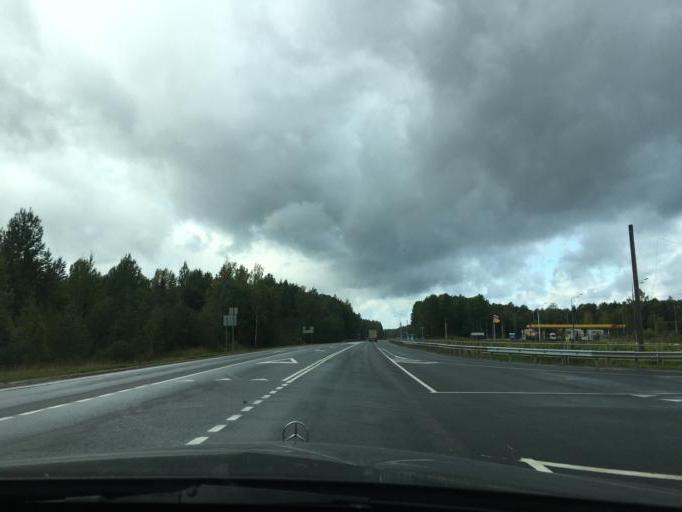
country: RU
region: Tverskaya
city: Nelidovo
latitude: 56.2652
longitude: 32.8461
